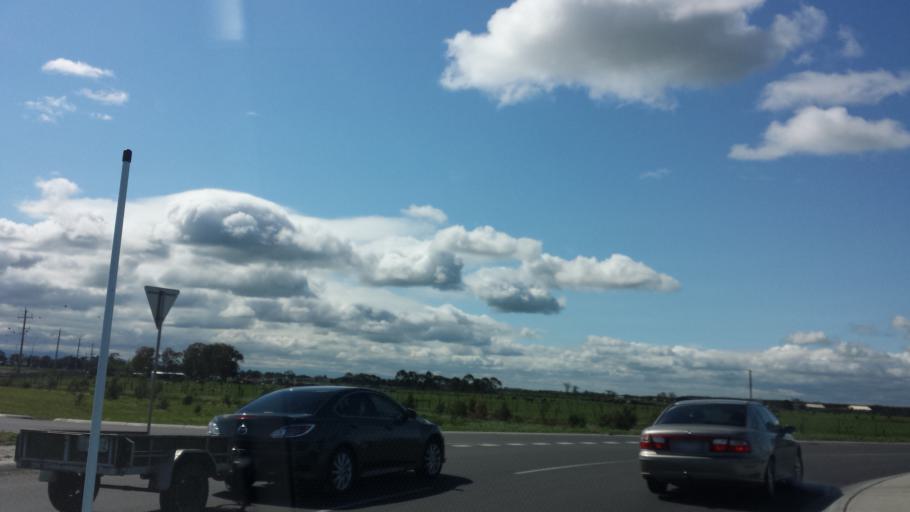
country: AU
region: Victoria
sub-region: Cardinia
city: Koo-Wee-Rup
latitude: -38.2111
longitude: 145.4695
